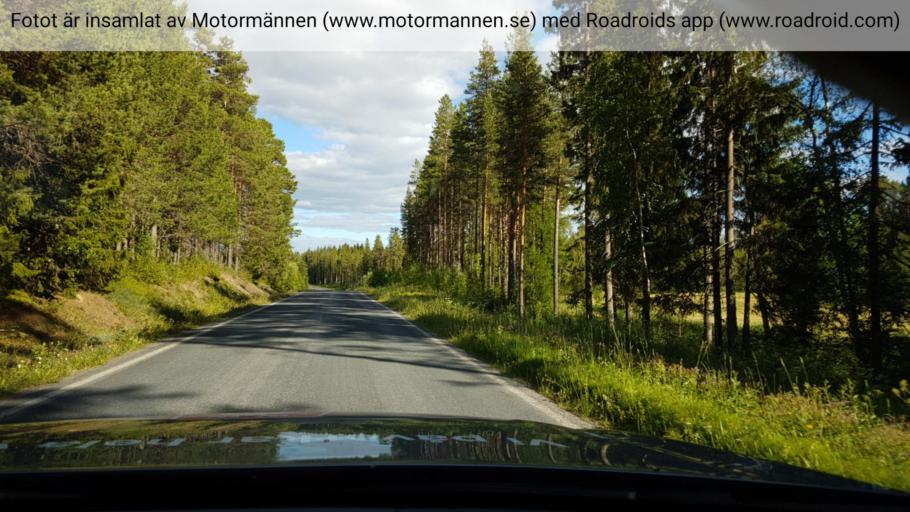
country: SE
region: Jaemtland
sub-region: Krokoms Kommun
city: Valla
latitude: 63.2884
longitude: 13.8725
